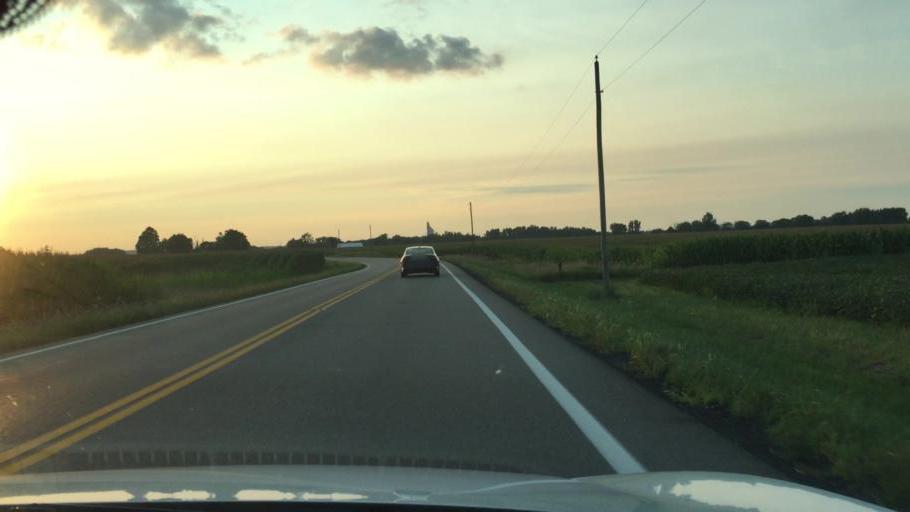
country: US
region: Ohio
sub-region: Champaign County
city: Mechanicsburg
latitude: 40.0593
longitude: -83.5363
